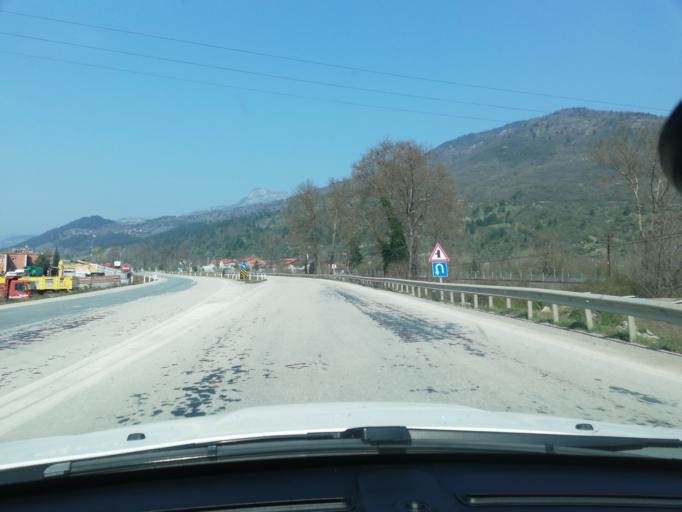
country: TR
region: Karabuk
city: Yenice
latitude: 41.2160
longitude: 32.3063
